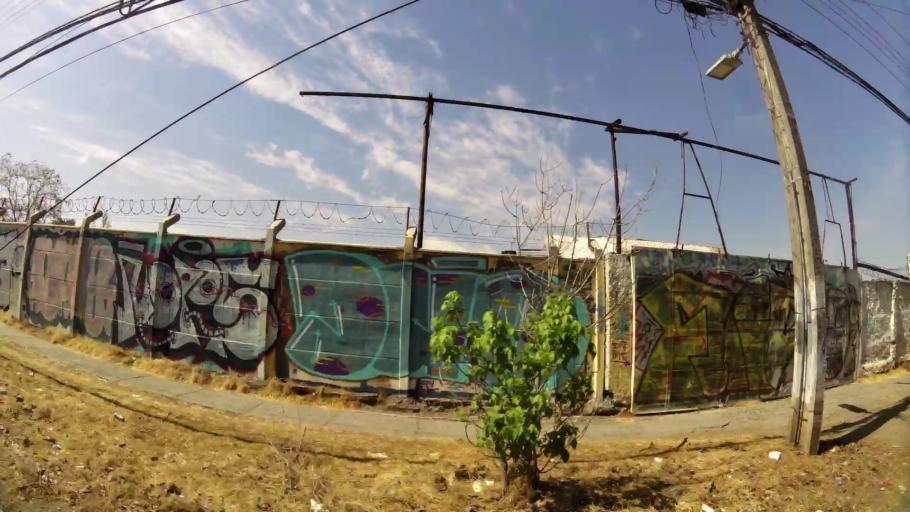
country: CL
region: Santiago Metropolitan
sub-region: Provincia de Santiago
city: La Pintana
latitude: -33.5440
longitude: -70.6633
